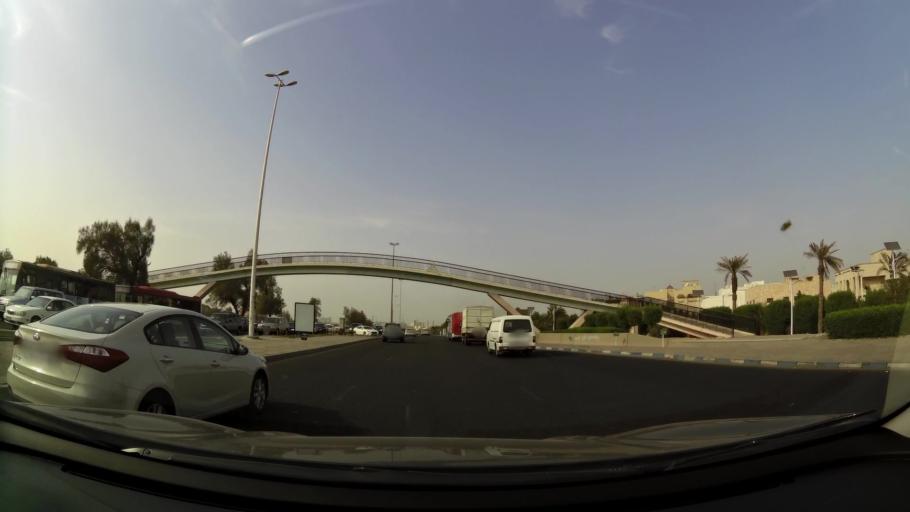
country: KW
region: Al Asimah
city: Ash Shamiyah
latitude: 29.3213
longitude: 47.9594
